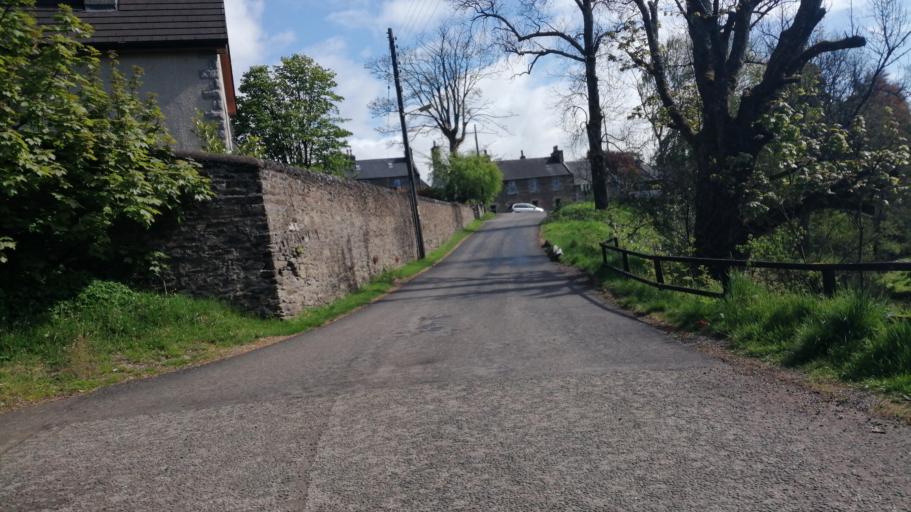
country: GB
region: Scotland
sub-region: Moray
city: Keith
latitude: 57.5434
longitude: -2.9594
